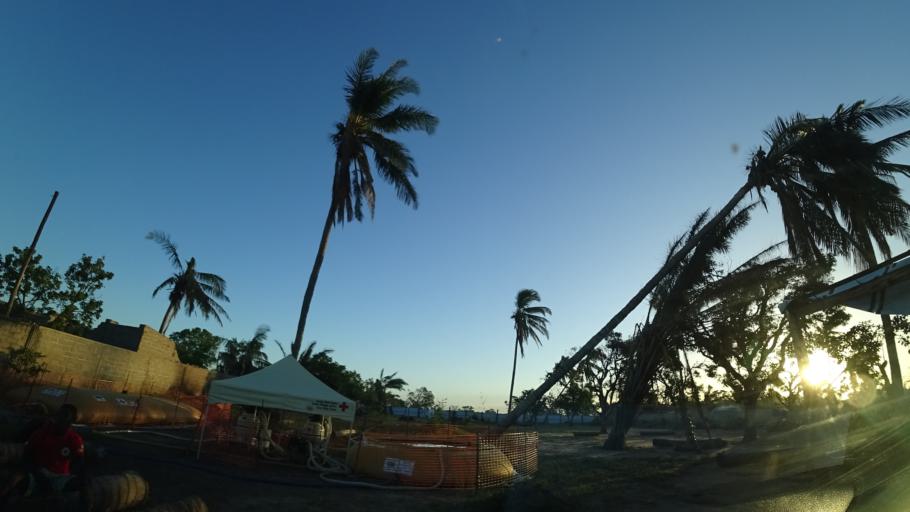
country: MZ
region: Sofala
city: Beira
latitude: -19.7322
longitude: 34.8254
